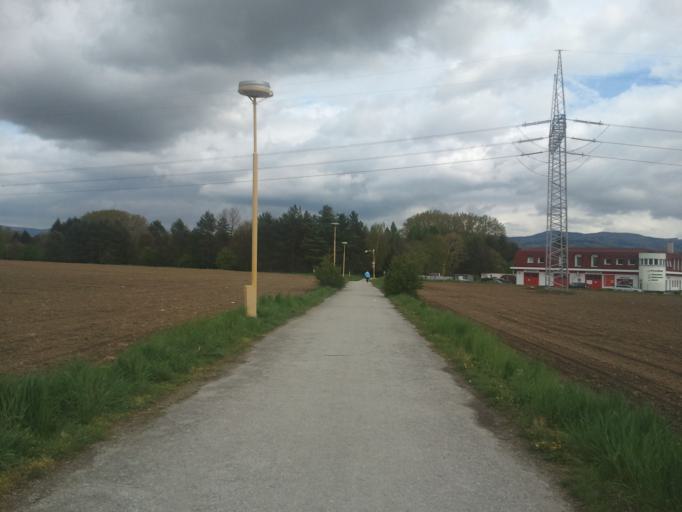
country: SK
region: Nitriansky
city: Bojnice
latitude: 48.7773
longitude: 18.5902
